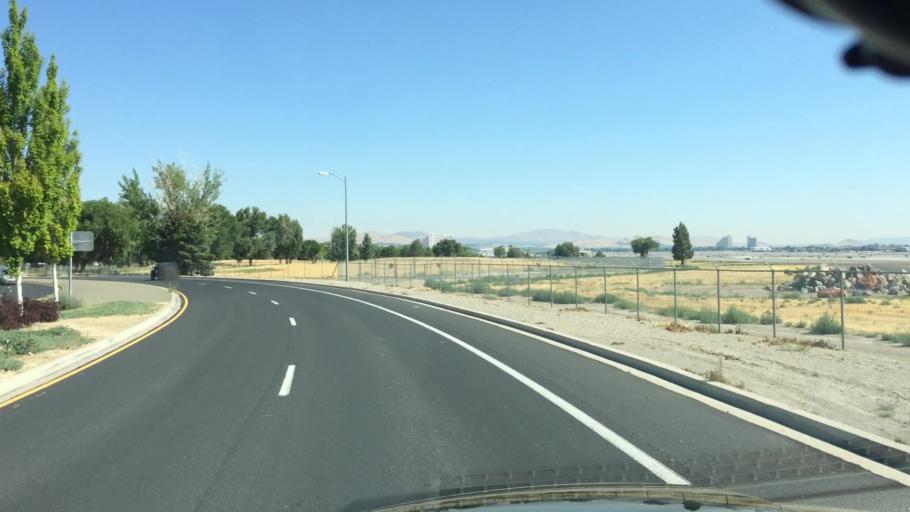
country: US
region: Nevada
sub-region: Washoe County
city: Sparks
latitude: 39.4826
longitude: -119.7731
